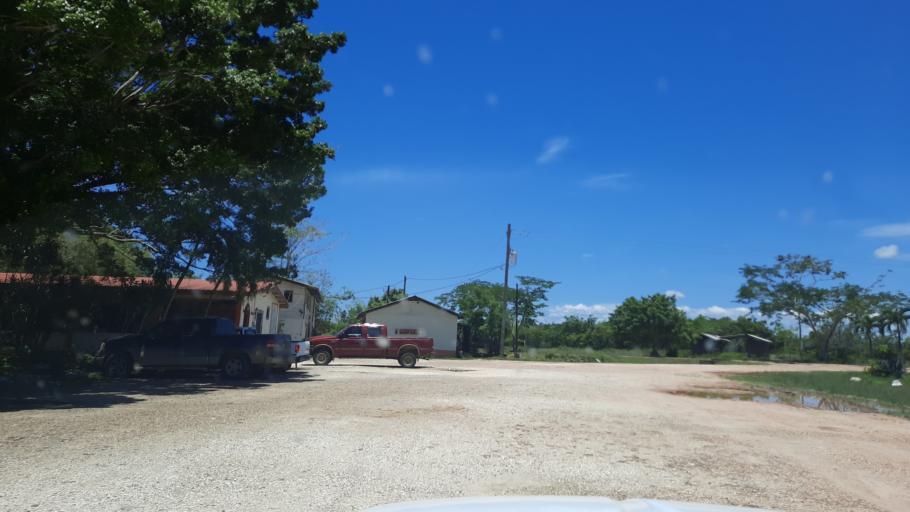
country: BZ
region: Cayo
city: Belmopan
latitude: 17.3240
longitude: -88.5648
